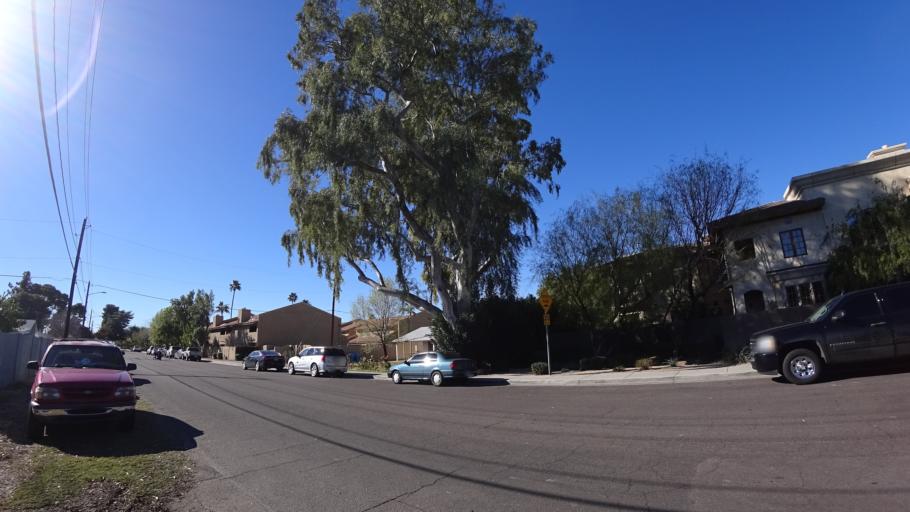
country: US
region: Arizona
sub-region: Maricopa County
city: Phoenix
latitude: 33.5012
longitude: -112.0345
